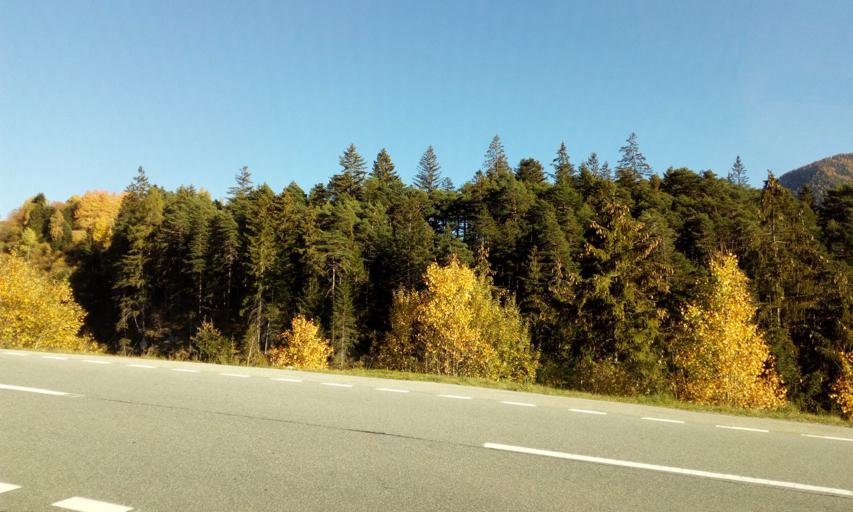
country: CH
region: Grisons
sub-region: Albula District
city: Tiefencastel
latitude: 46.6724
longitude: 9.6304
